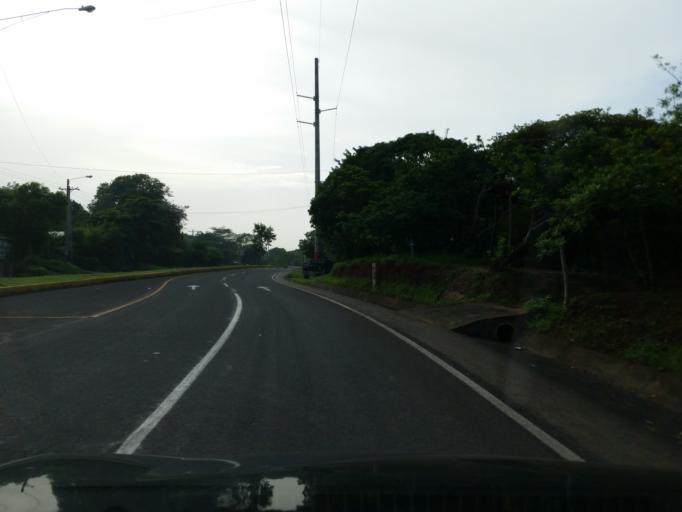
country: NI
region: Granada
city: Granada
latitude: 11.9670
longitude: -86.0130
